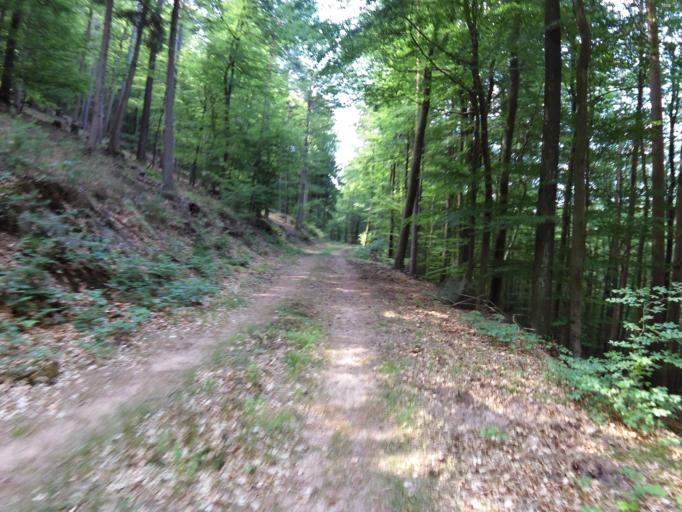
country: DE
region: Rheinland-Pfalz
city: Waldleiningen
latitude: 49.3796
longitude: 7.8598
